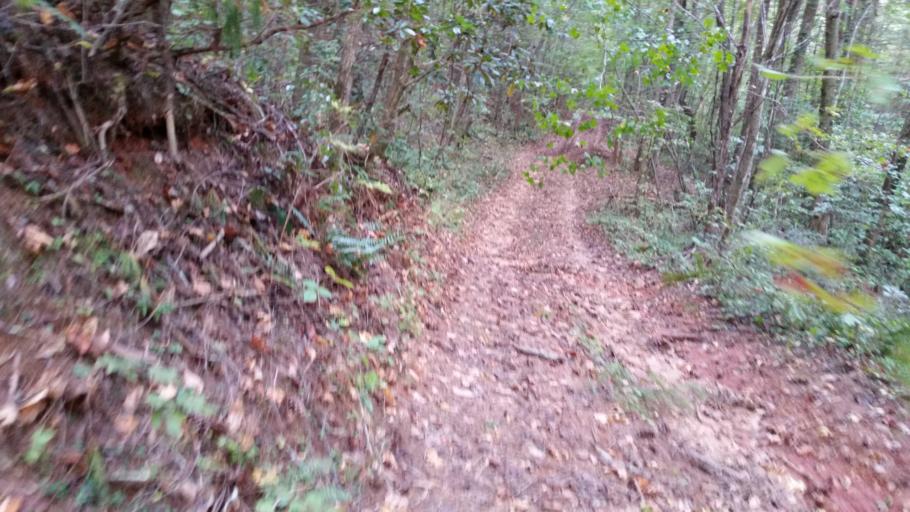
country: US
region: Georgia
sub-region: Dawson County
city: Dawsonville
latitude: 34.5776
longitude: -84.1809
